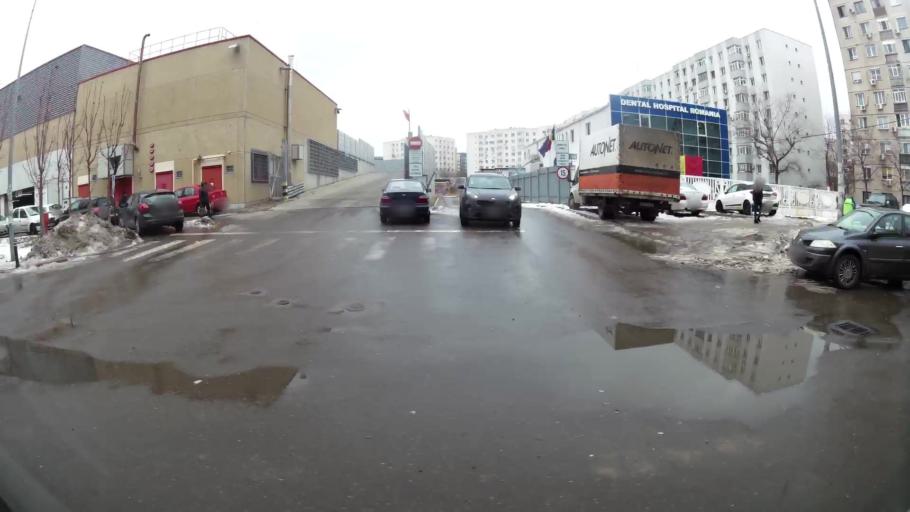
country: RO
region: Bucuresti
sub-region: Municipiul Bucuresti
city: Bucharest
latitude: 44.4142
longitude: 26.1359
